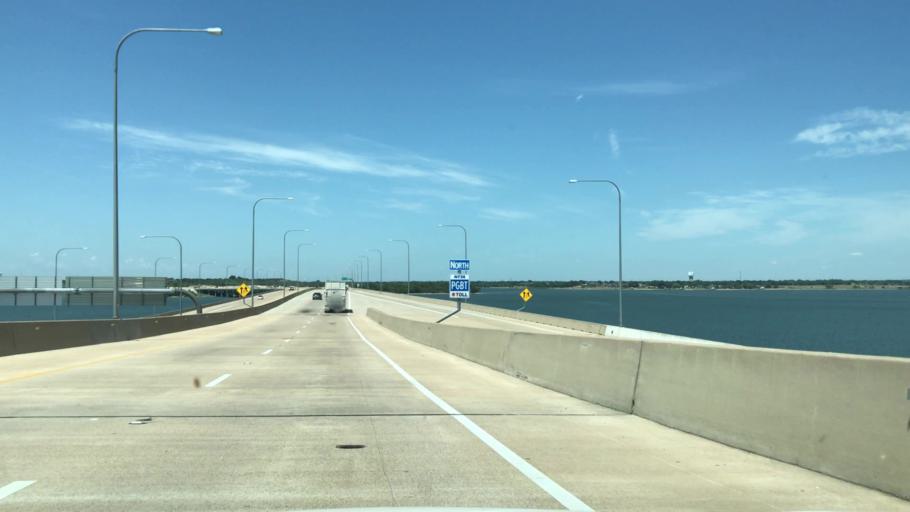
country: US
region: Texas
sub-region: Dallas County
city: Rowlett
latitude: 32.8636
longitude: -96.5545
